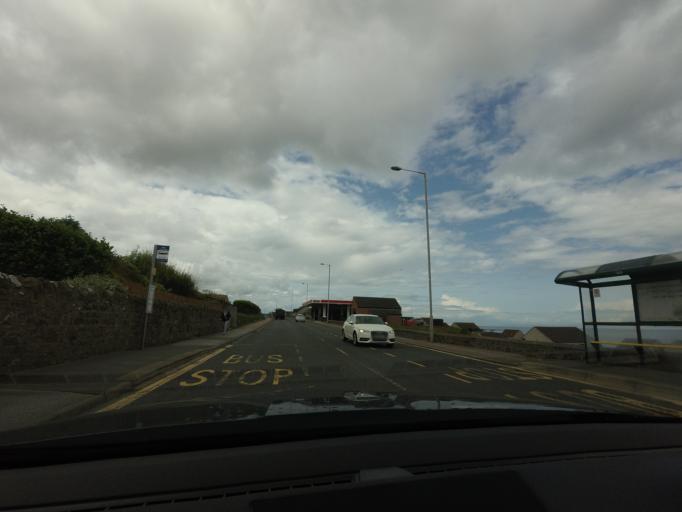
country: GB
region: Scotland
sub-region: Aberdeenshire
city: Banff
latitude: 57.6678
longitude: -2.5355
